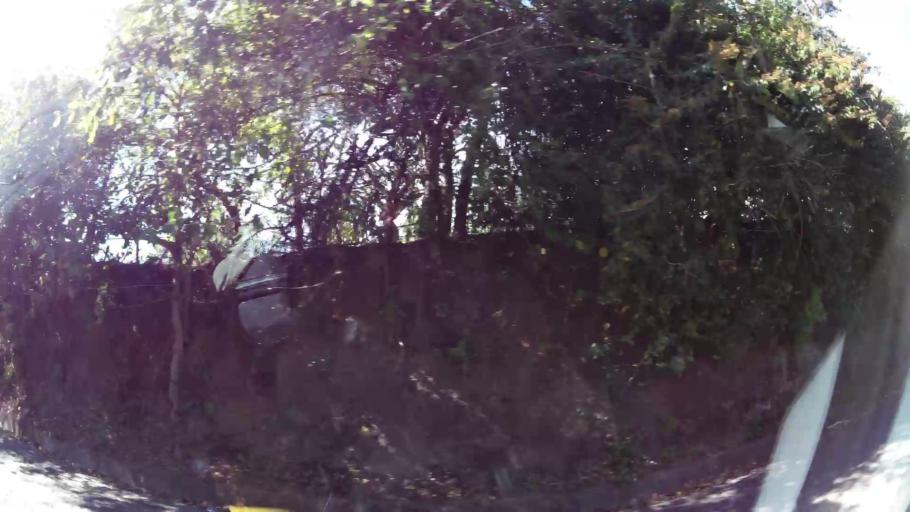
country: SV
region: Cuscatlan
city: Suchitoto
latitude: 13.9298
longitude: -89.0320
